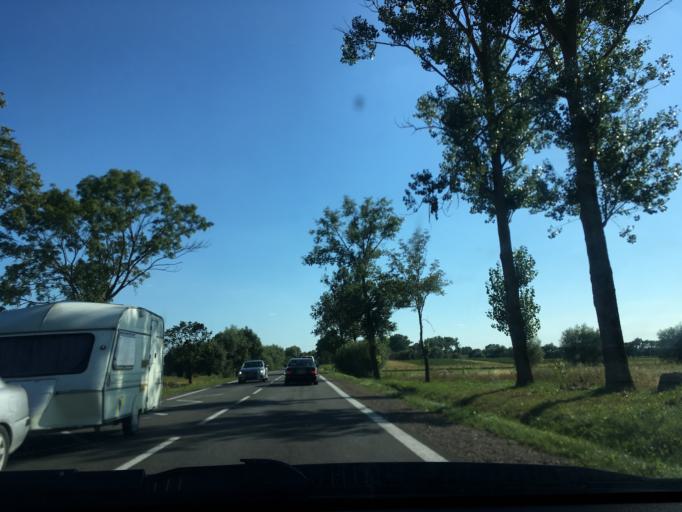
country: PL
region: Podlasie
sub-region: Powiat sokolski
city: Suchowola
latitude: 53.5177
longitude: 23.1050
